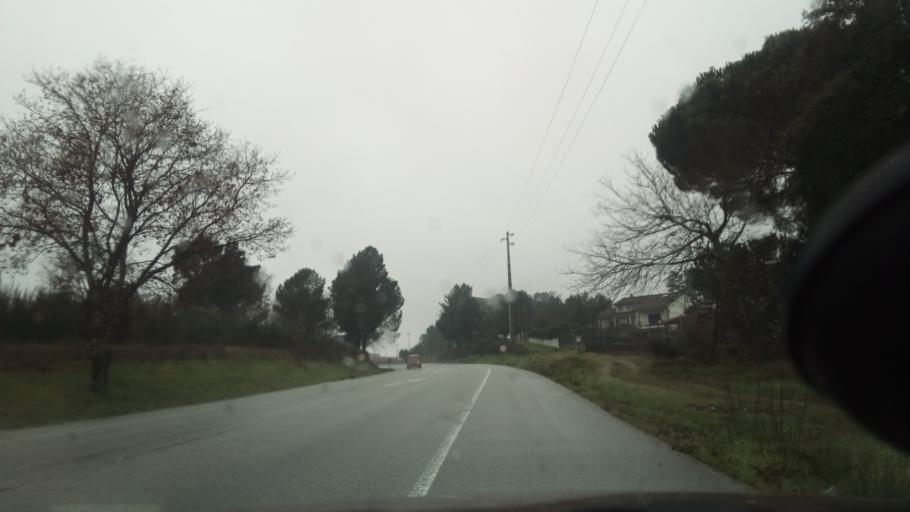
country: PT
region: Viseu
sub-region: Mangualde
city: Mangualde
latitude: 40.6144
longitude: -7.7721
